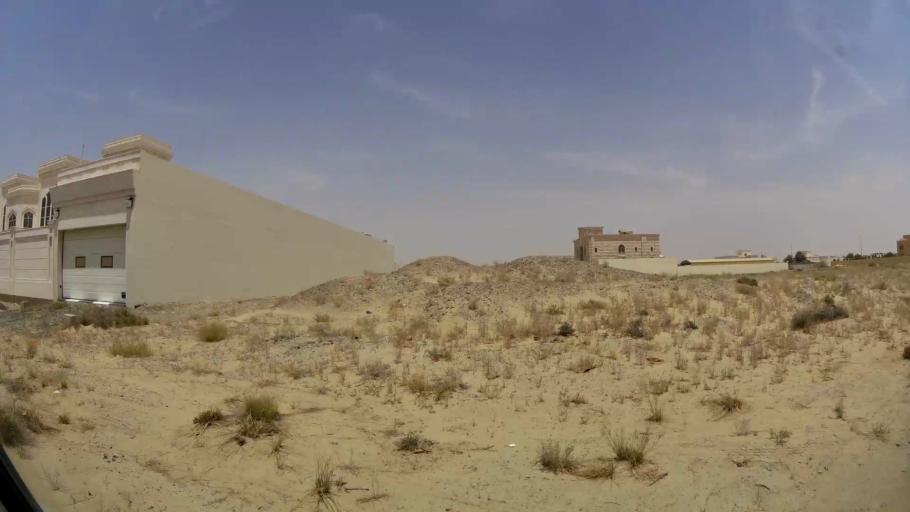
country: AE
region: Ash Shariqah
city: Sharjah
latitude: 25.2462
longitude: 55.4709
